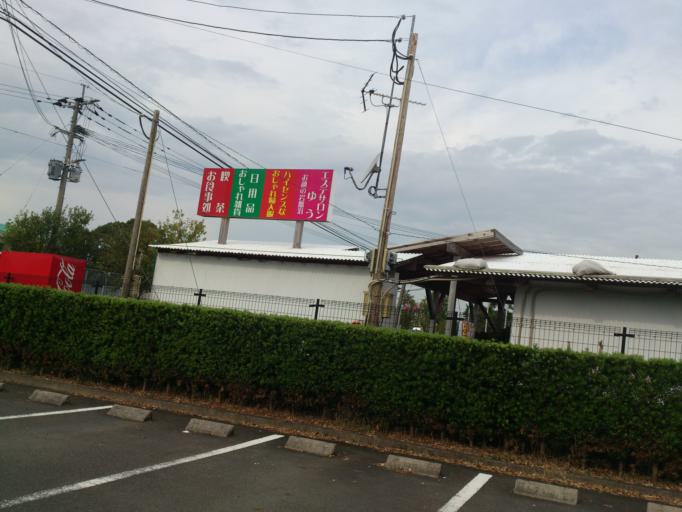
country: JP
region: Kagoshima
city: Kanoya
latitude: 31.3520
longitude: 130.9464
